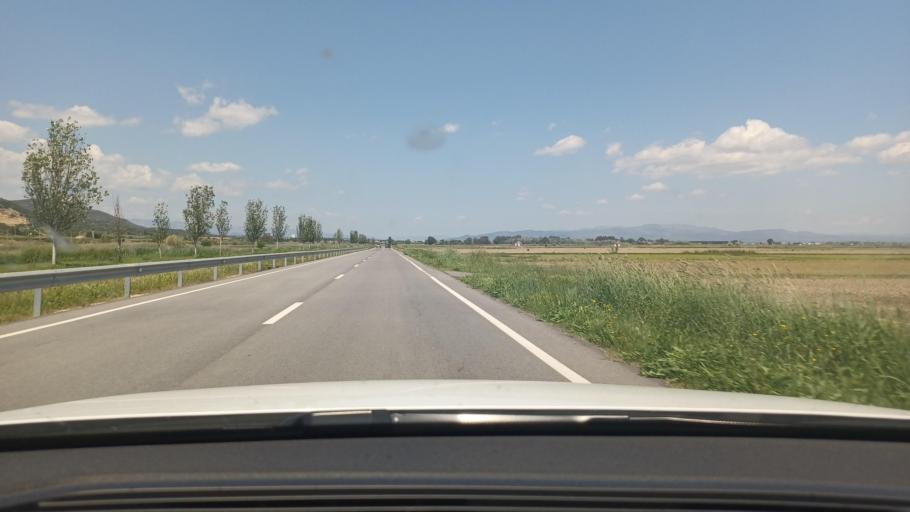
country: ES
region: Catalonia
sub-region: Provincia de Tarragona
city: Sant Carles de la Rapita
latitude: 40.6519
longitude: 0.5961
